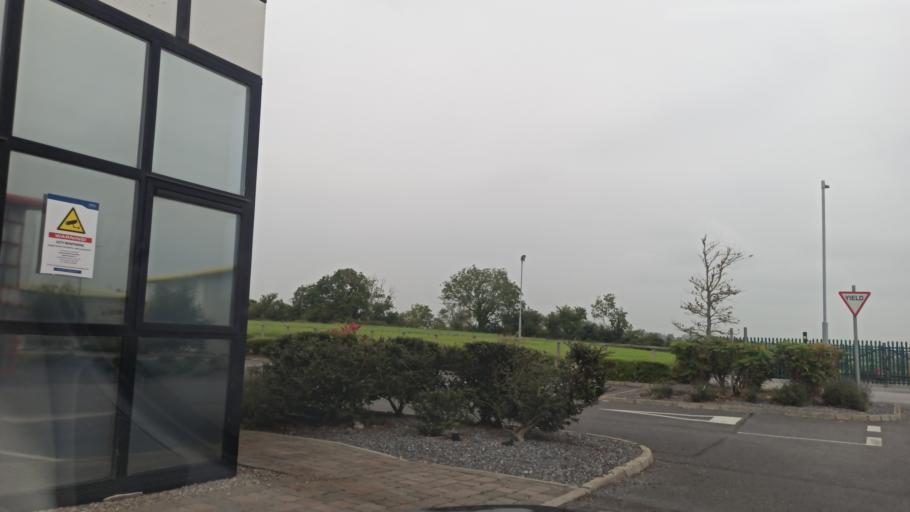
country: IE
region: Munster
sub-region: South Tipperary
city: Cluain Meala
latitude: 52.3743
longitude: -7.7247
